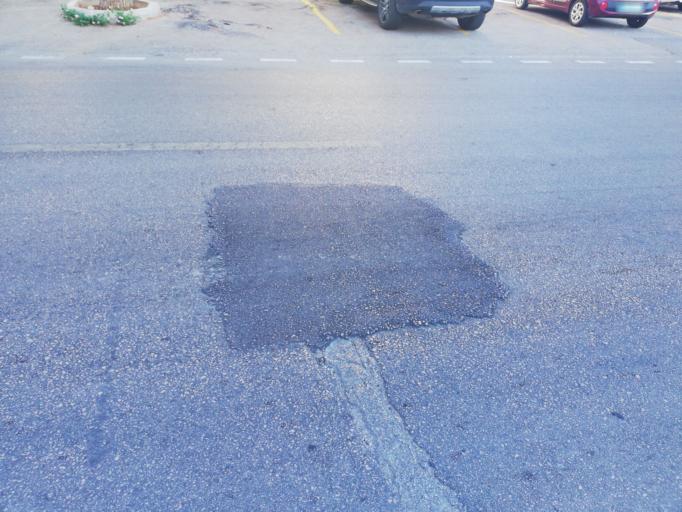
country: LB
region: Mont-Liban
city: Jdaidet el Matn
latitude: 33.8981
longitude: 35.5972
